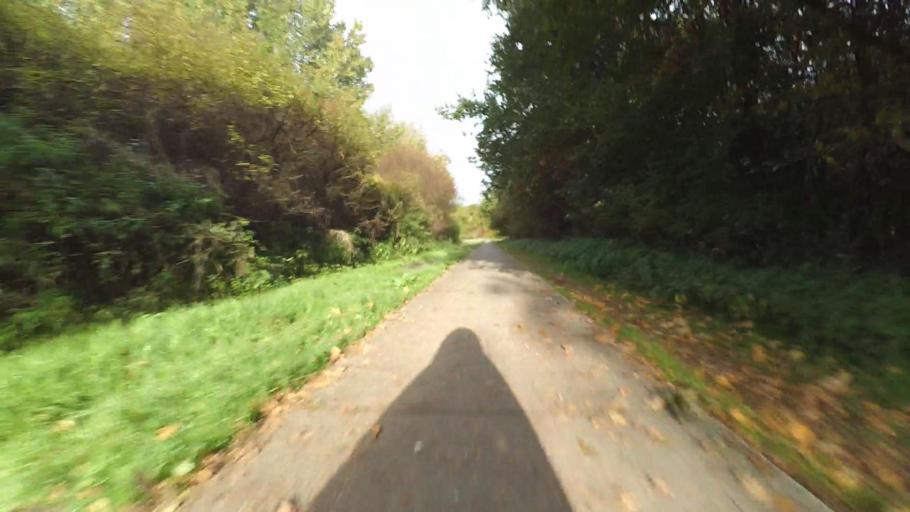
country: NL
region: North Holland
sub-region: Gemeente Huizen
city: Huizen
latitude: 52.3303
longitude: 5.3020
